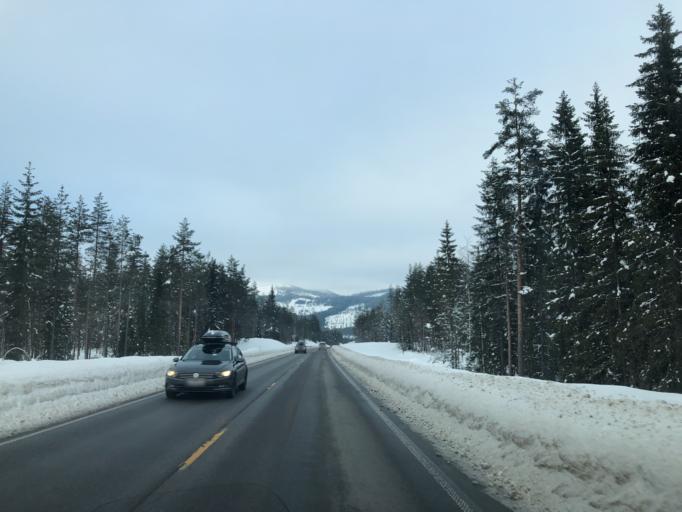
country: NO
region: Hedmark
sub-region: Trysil
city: Innbygda
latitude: 61.2539
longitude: 12.3003
